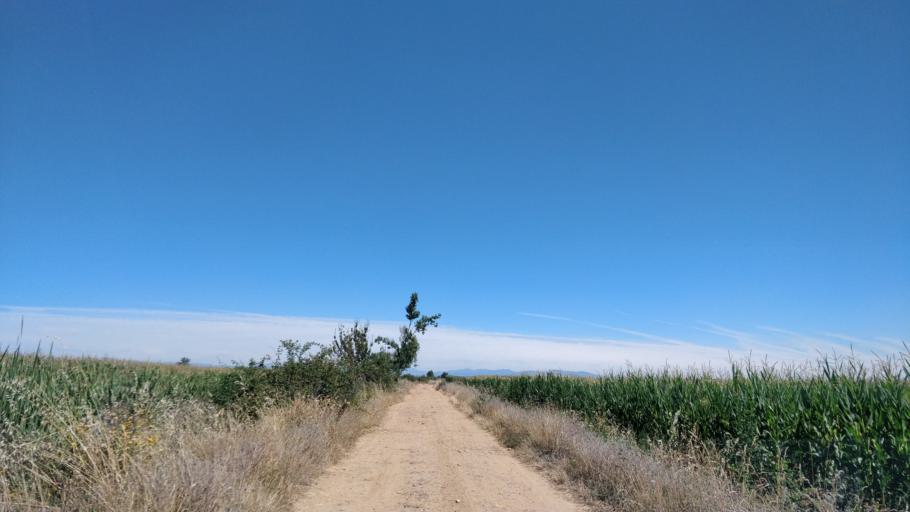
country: ES
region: Castille and Leon
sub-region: Provincia de Leon
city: Bustillo del Paramo
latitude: 42.4413
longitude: -5.8150
